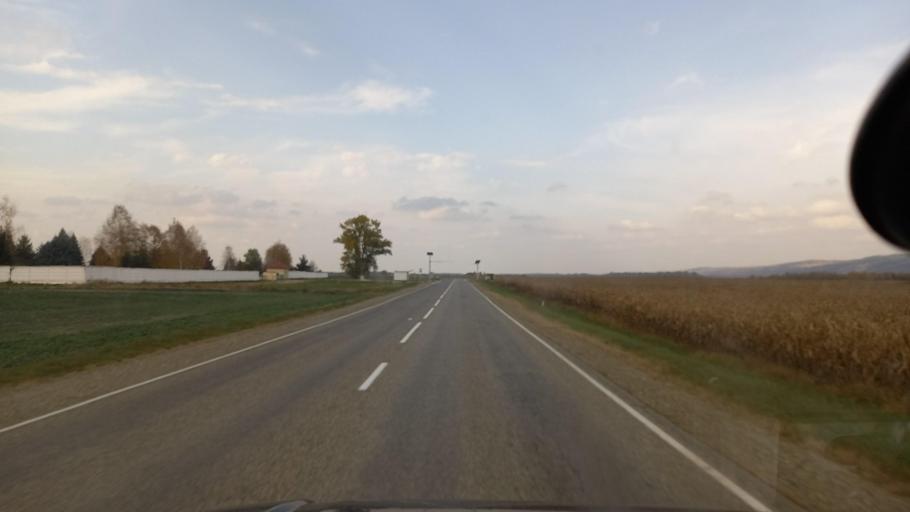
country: RU
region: Krasnodarskiy
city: Perepravnaya
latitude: 44.3472
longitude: 40.8412
